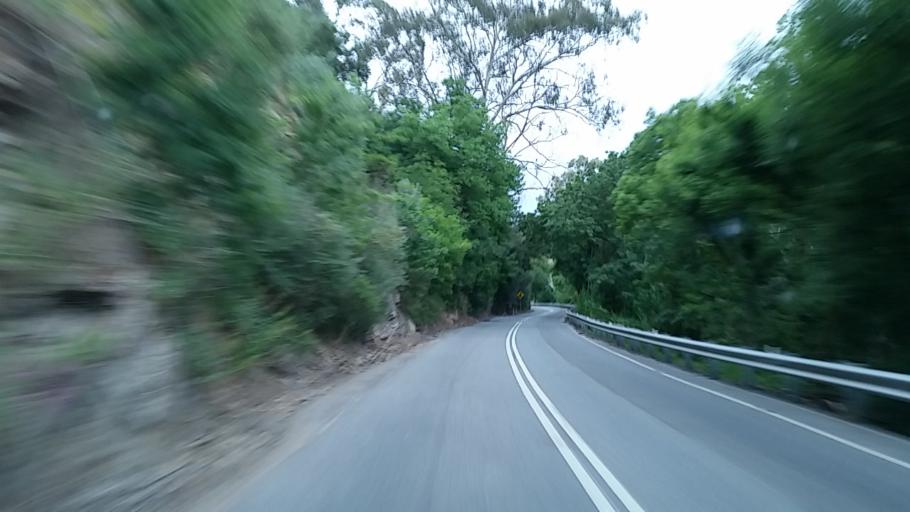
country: AU
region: South Australia
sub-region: Campbelltown
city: Athelstone
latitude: -34.8650
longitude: 138.7484
